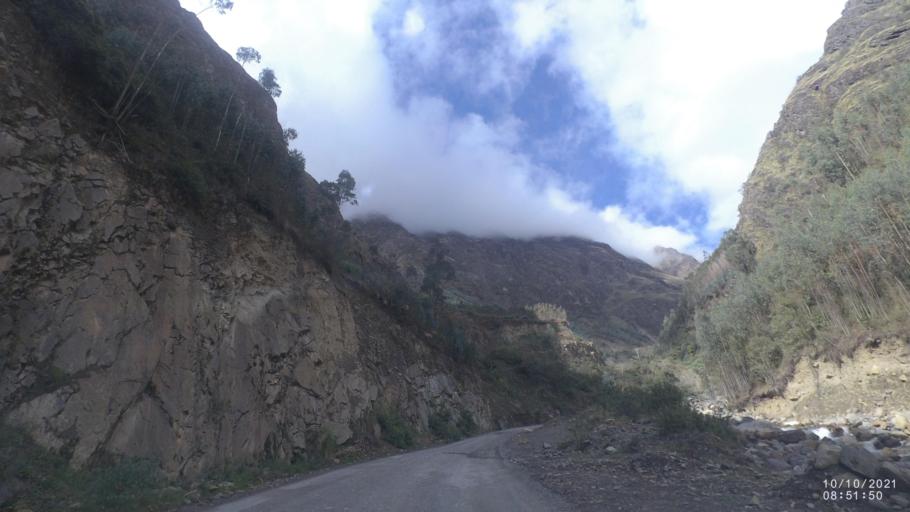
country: BO
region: La Paz
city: Quime
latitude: -16.9843
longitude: -67.2277
